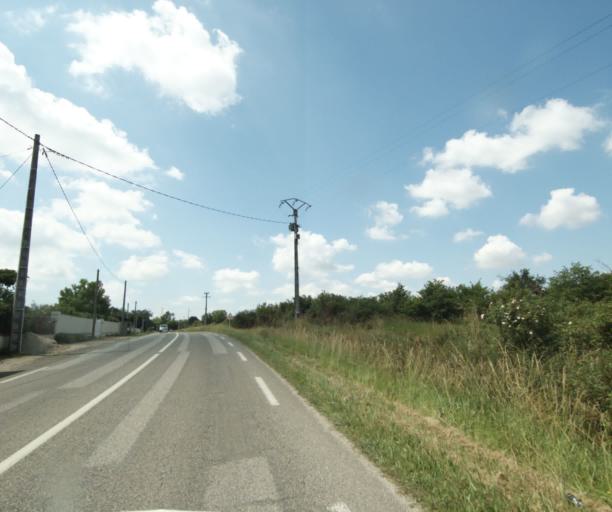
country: FR
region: Midi-Pyrenees
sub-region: Departement du Tarn-et-Garonne
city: Montauban
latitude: 44.0575
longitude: 1.3602
